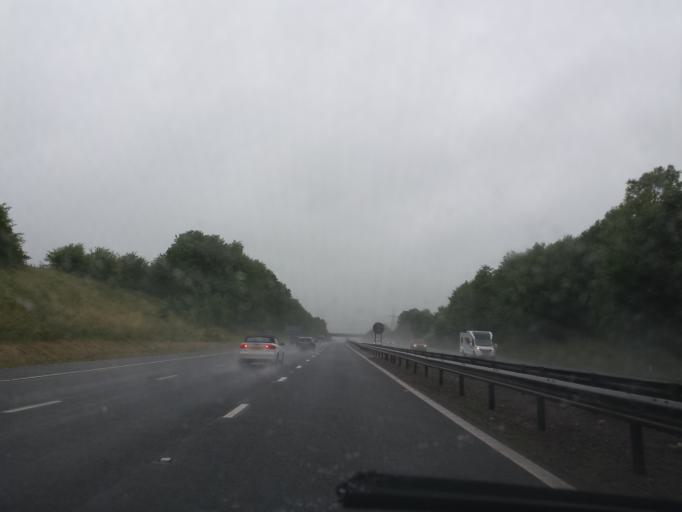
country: GB
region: England
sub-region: Leicestershire
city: Enderby
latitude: 52.5947
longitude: -1.2189
